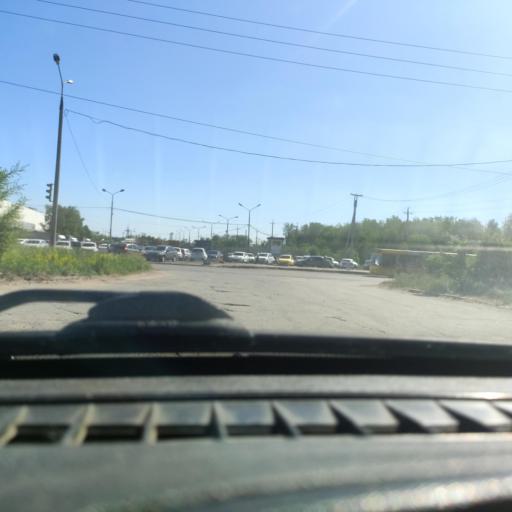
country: RU
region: Samara
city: Podstepki
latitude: 53.5843
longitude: 49.2307
